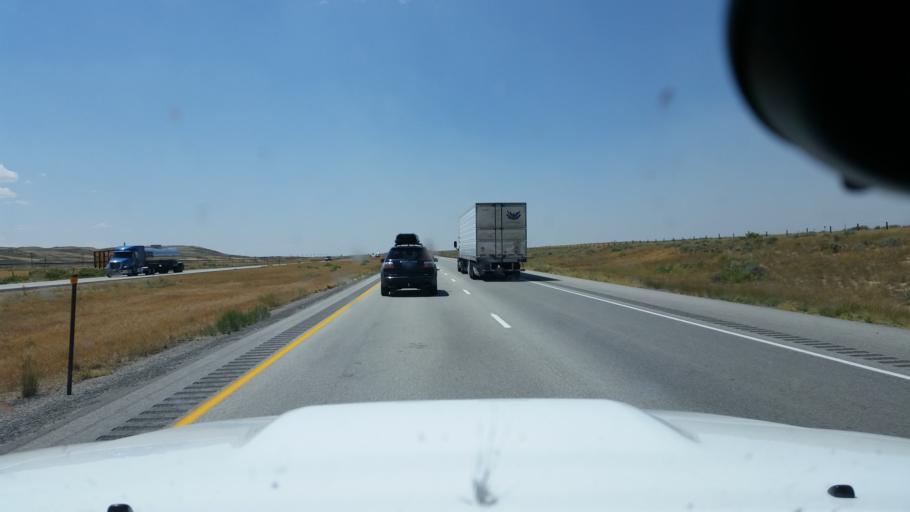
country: US
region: Wyoming
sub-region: Sweetwater County
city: Rock Springs
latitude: 41.6385
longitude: -108.2298
